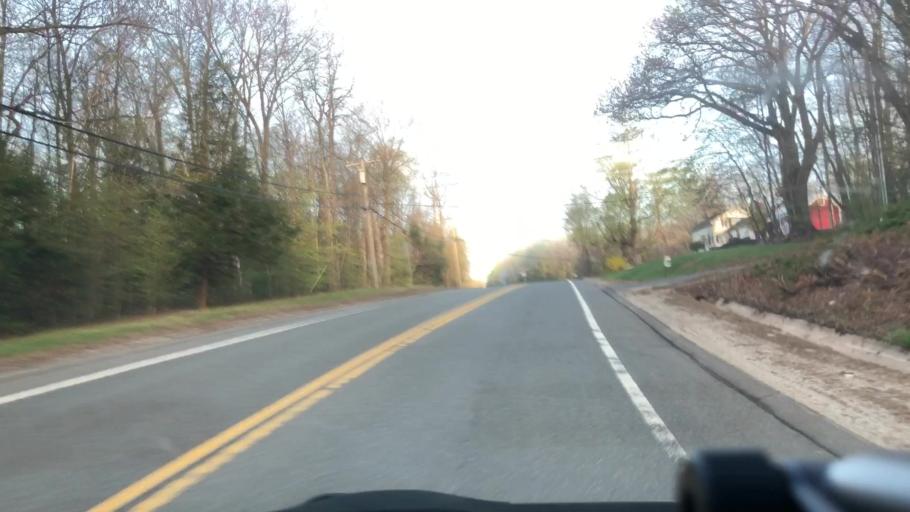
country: US
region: Massachusetts
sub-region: Hampshire County
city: Westhampton
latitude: 42.2835
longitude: -72.8101
